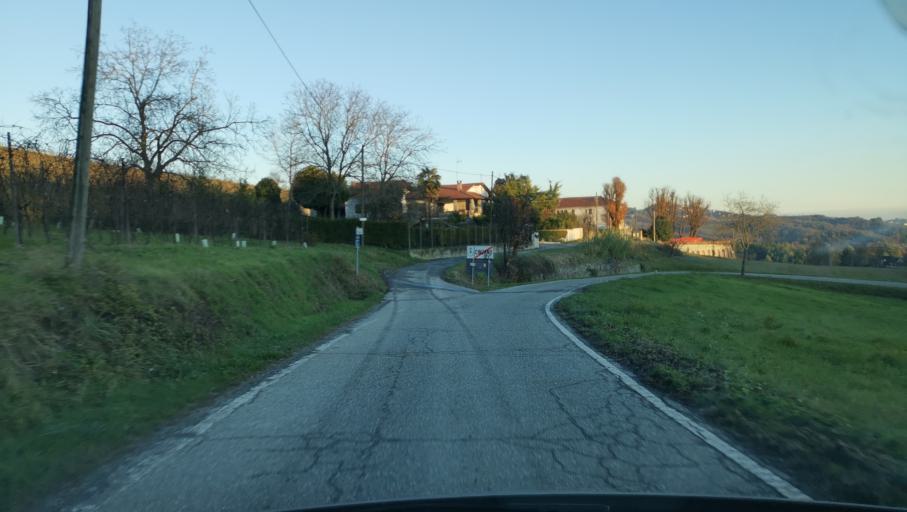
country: IT
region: Piedmont
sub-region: Provincia di Torino
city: Cinzano
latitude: 45.0903
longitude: 7.9244
